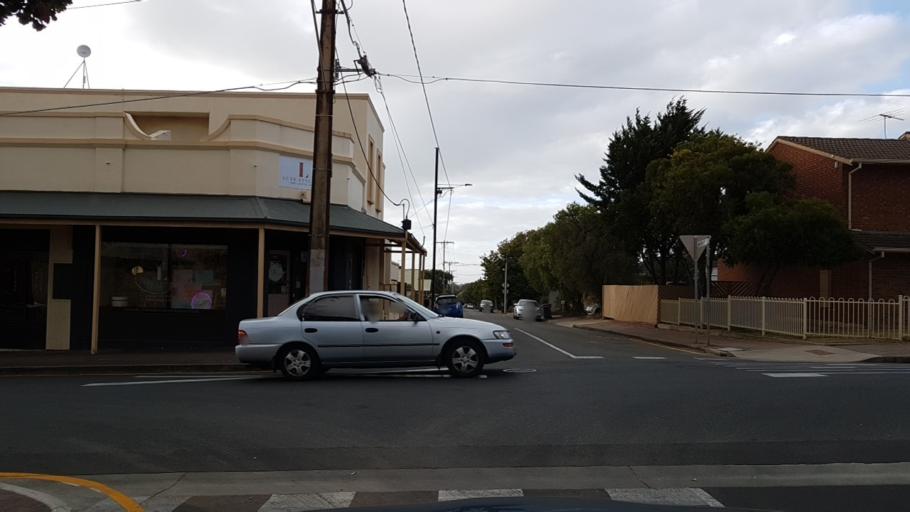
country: AU
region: South Australia
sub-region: Adelaide Hills
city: Seacliff
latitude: -35.0318
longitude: 138.5204
